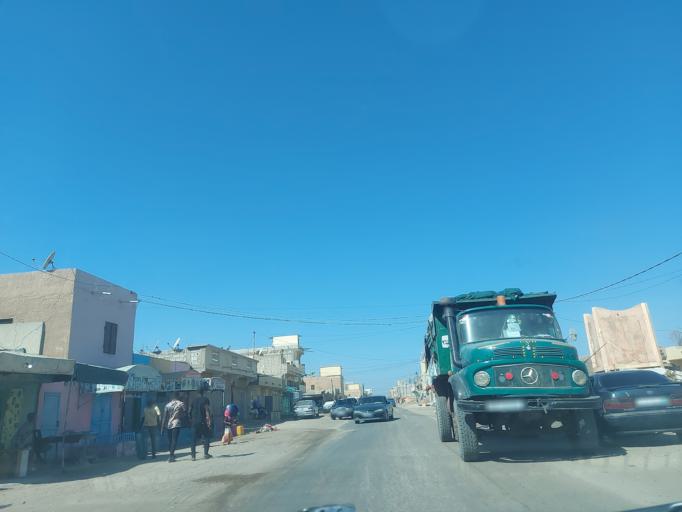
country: MR
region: Nouakchott
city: Nouakchott
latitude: 18.0779
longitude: -15.9935
